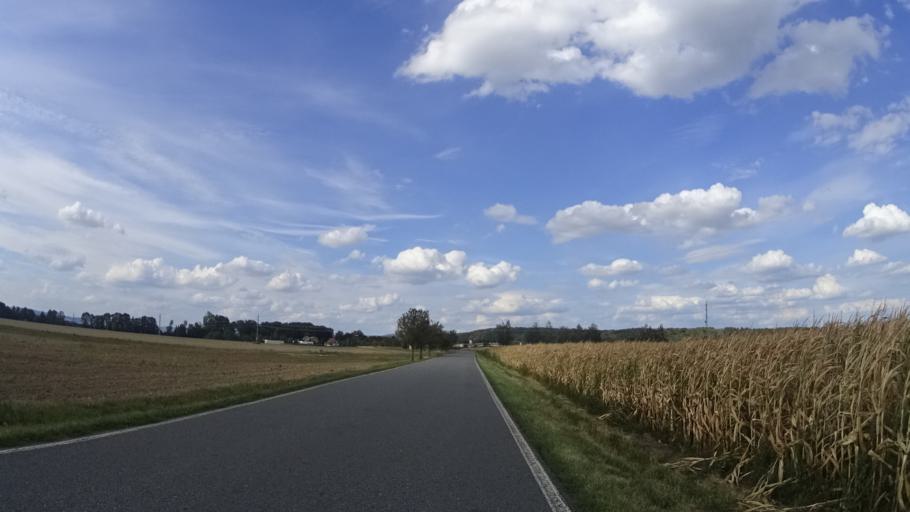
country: CZ
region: Olomoucky
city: Moravicany
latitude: 49.7383
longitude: 16.9738
